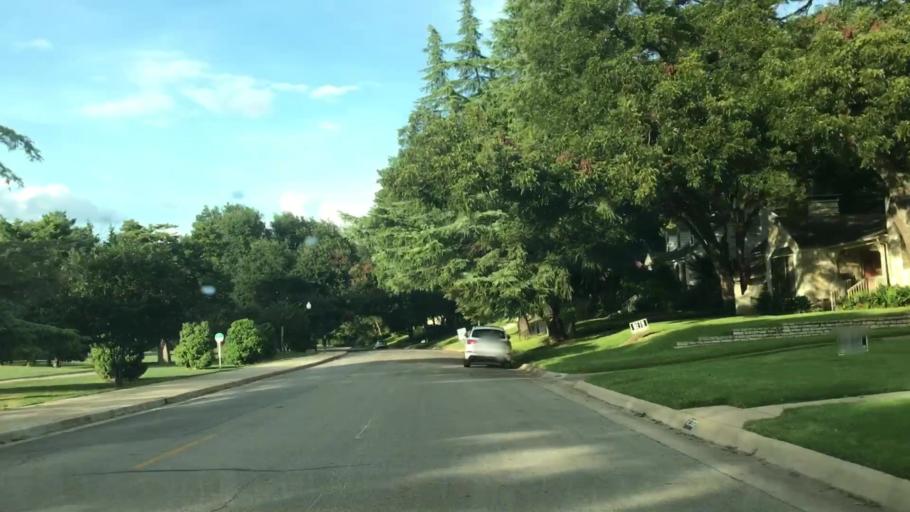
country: US
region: Texas
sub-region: Dallas County
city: Cockrell Hill
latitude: 32.7600
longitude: -96.8471
